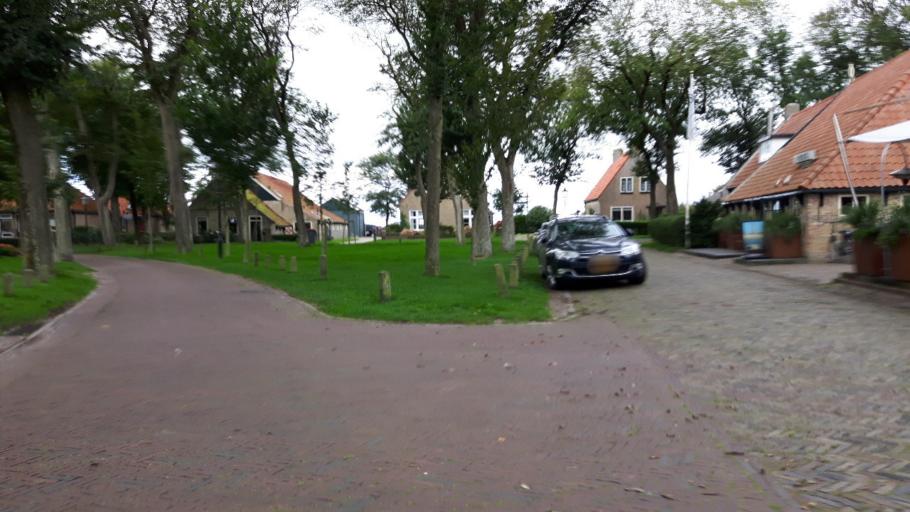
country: NL
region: Friesland
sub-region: Gemeente Ameland
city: Hollum
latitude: 53.4436
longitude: 5.6875
